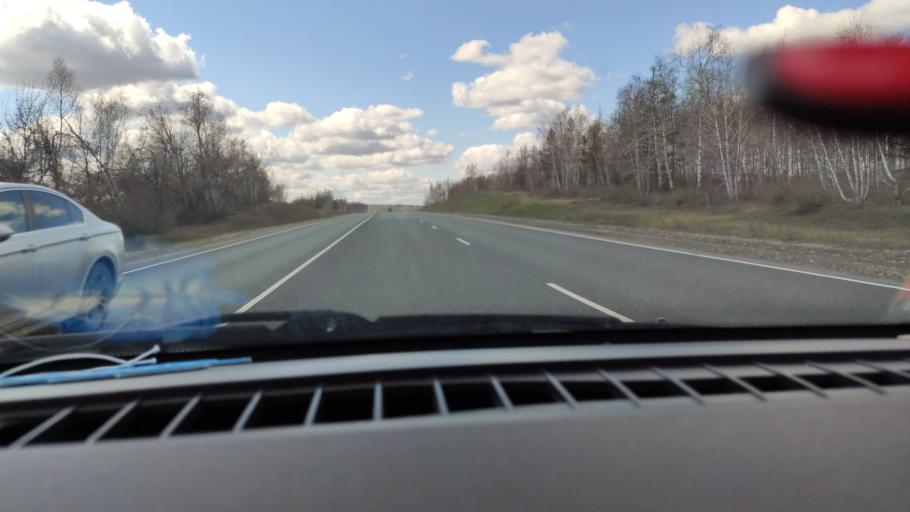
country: RU
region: Saratov
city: Khvalynsk
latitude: 52.5560
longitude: 48.0821
